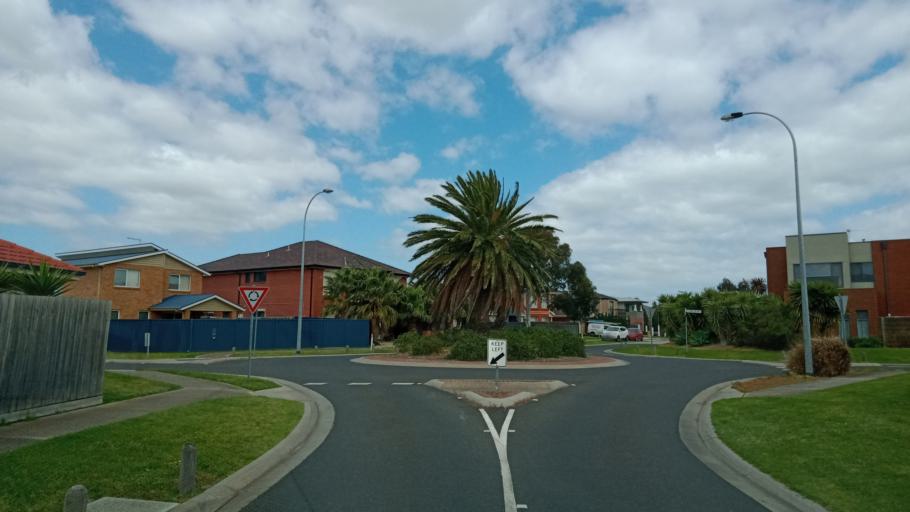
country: AU
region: Victoria
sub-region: Kingston
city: Patterson Lakes
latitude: -38.0599
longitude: 145.1414
